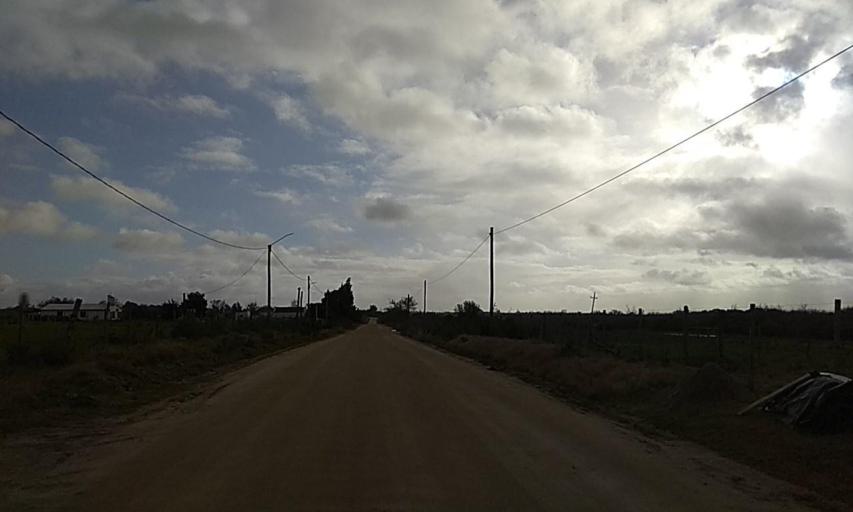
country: UY
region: Florida
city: Florida
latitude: -34.0603
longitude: -56.1920
